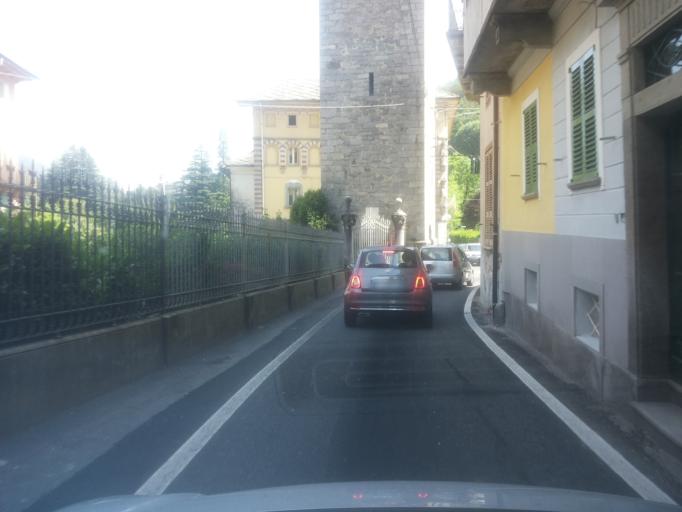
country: IT
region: Piedmont
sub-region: Provincia di Biella
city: Rosazza
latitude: 45.6766
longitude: 7.9772
